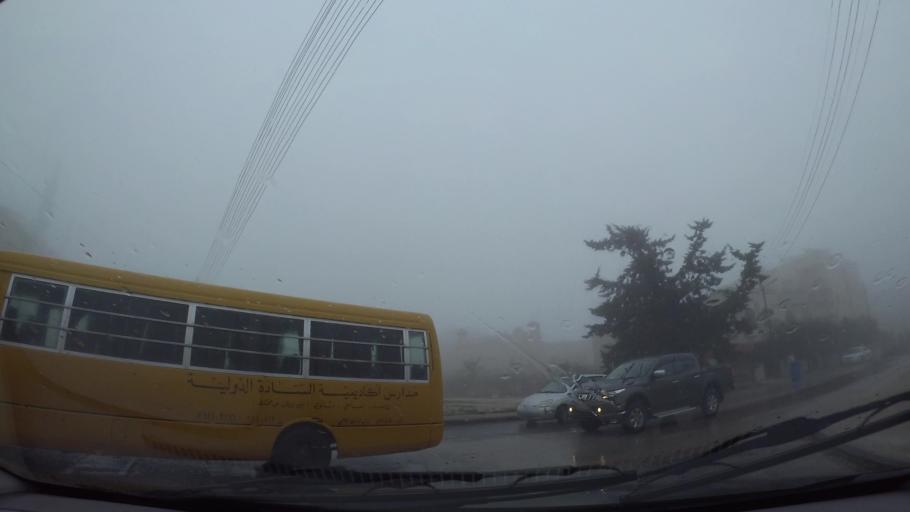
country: JO
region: Amman
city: Al Jubayhah
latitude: 32.0091
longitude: 35.8827
